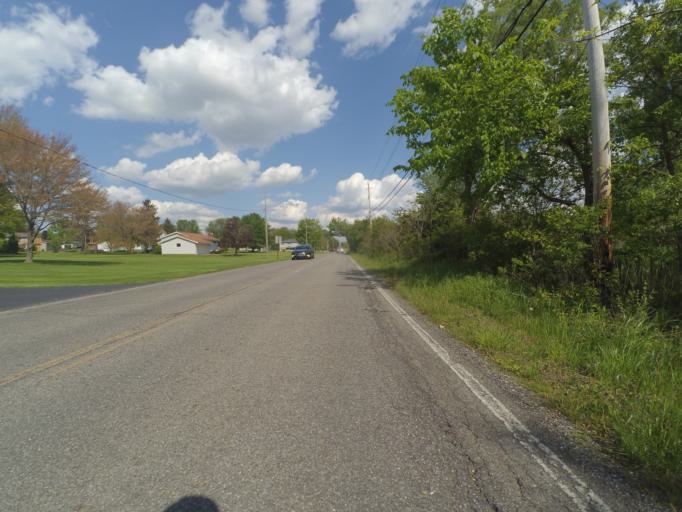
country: US
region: Ohio
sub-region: Trumbull County
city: Mineral Ridge
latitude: 41.1340
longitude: -80.7552
